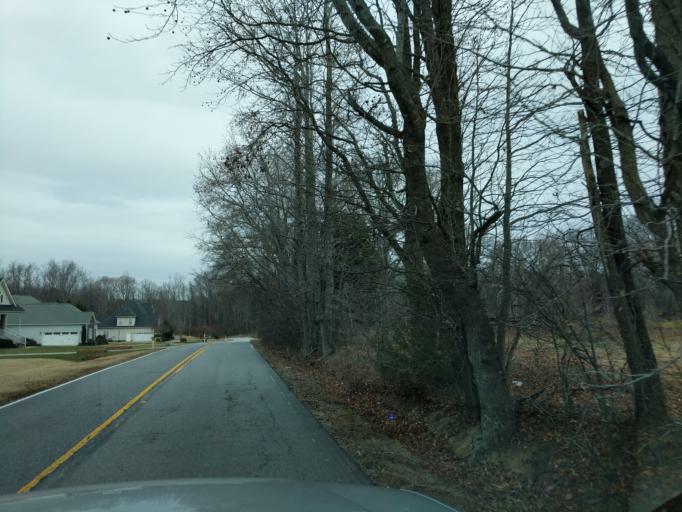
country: US
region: South Carolina
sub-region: Spartanburg County
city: Duncan
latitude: 34.8669
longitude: -82.1268
